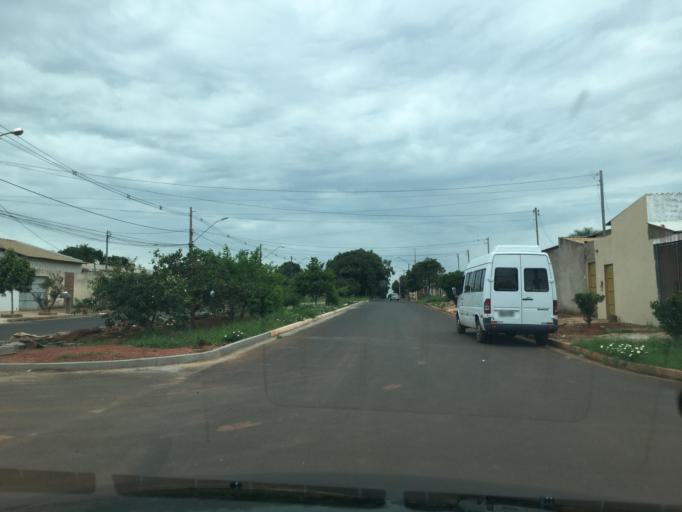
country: BR
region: Minas Gerais
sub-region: Uberlandia
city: Uberlandia
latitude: -18.8728
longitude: -48.2256
